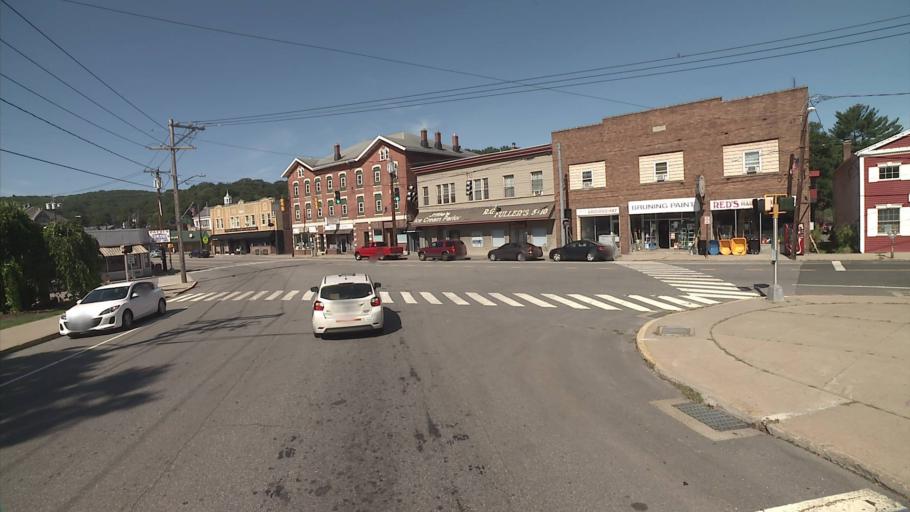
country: US
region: Connecticut
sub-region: Litchfield County
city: Thomaston
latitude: 41.6742
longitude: -73.0727
